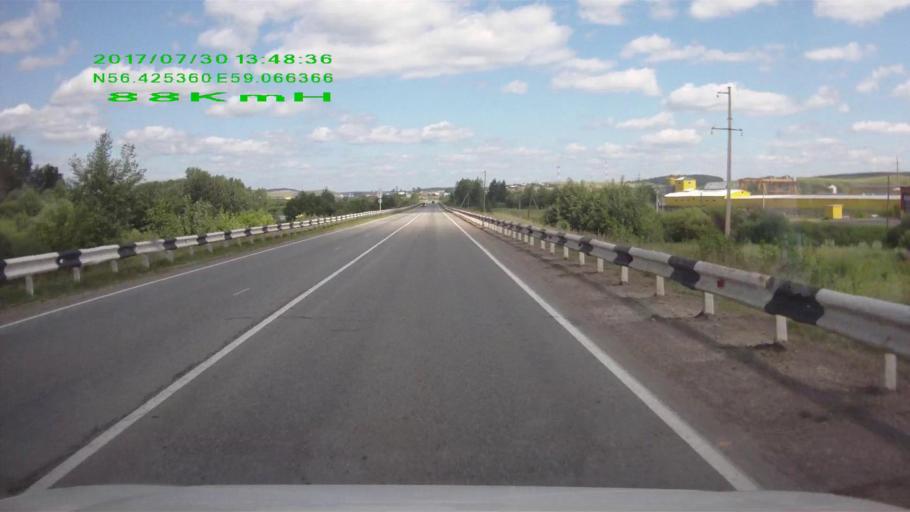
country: RU
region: Sverdlovsk
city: Mikhaylovsk
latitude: 56.4257
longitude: 59.0672
